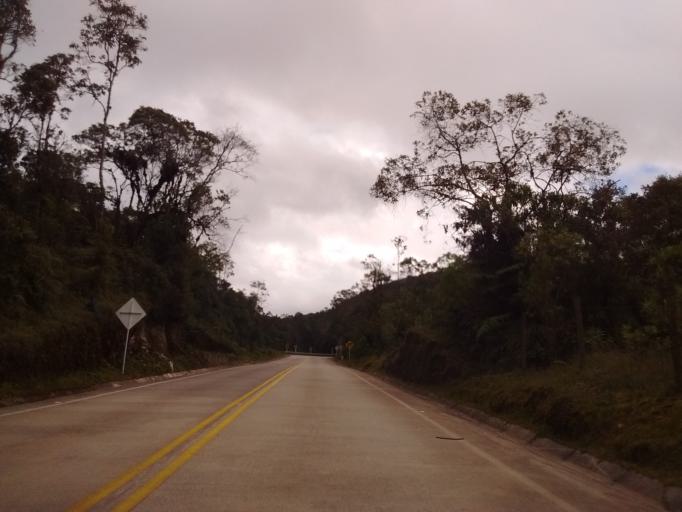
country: CO
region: Huila
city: Isnos
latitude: 2.0443
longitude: -76.2909
